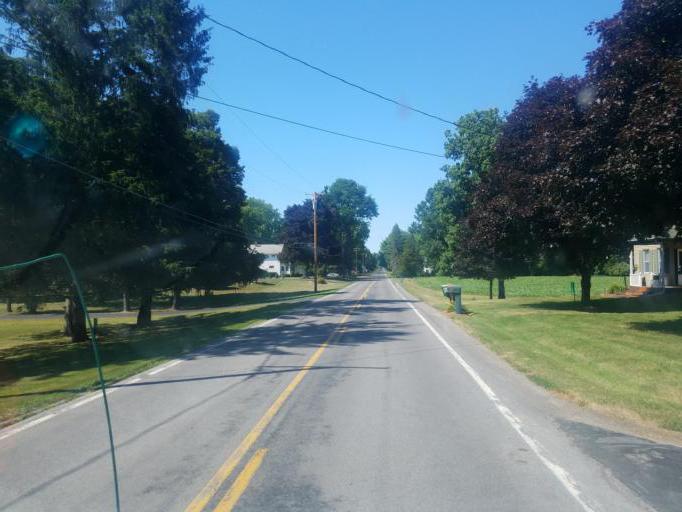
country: US
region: New York
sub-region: Ontario County
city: Geneva
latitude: 42.9280
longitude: -76.9992
